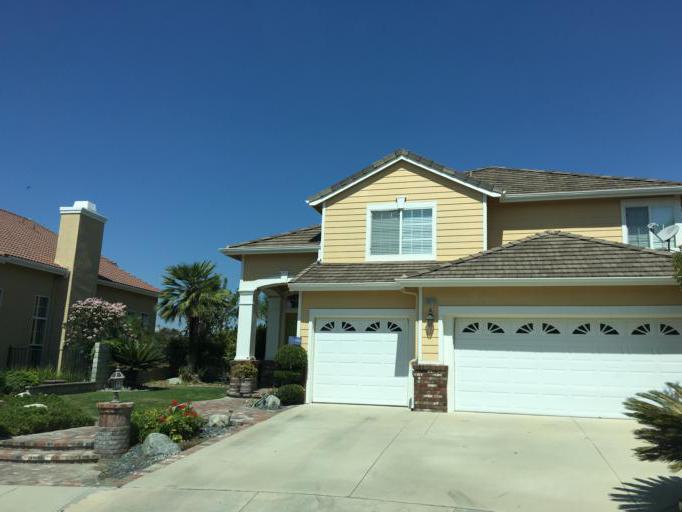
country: US
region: California
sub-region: Los Angeles County
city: Santa Clarita
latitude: 34.3961
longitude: -118.5921
